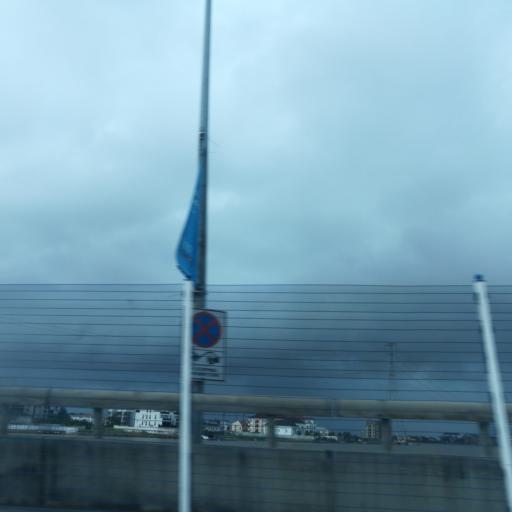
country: NG
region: Lagos
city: Ikoyi
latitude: 6.4487
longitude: 3.4595
